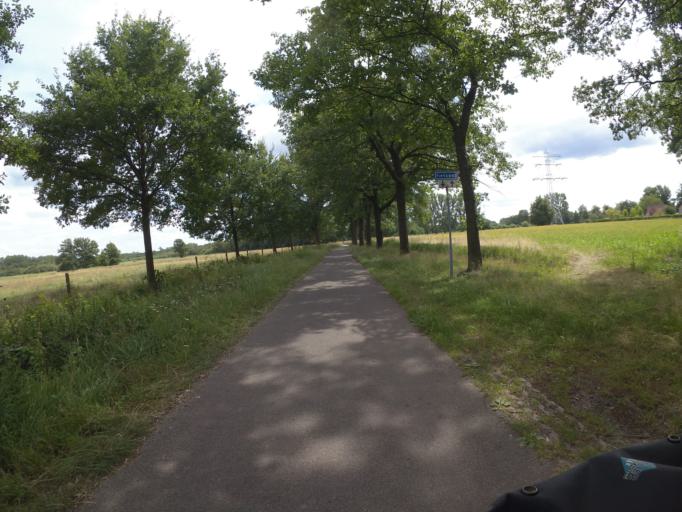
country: NL
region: North Brabant
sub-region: Gemeente Eindhoven
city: Muschberg en Geestenberg
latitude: 51.4381
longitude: 5.5355
